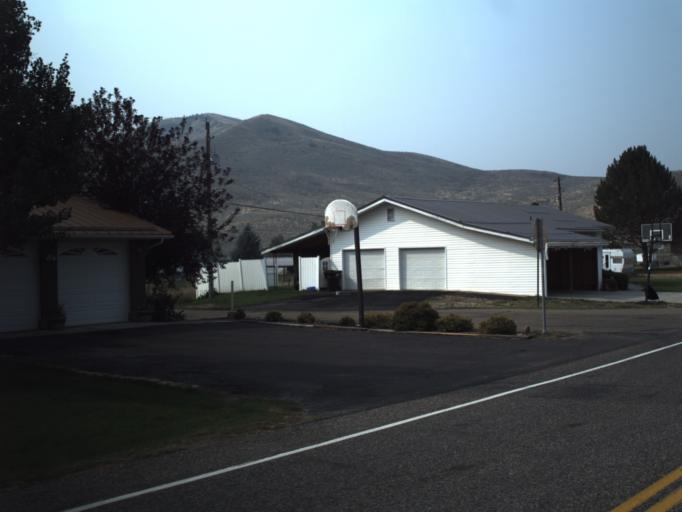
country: US
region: Utah
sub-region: Summit County
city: Coalville
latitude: 41.0196
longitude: -111.5033
